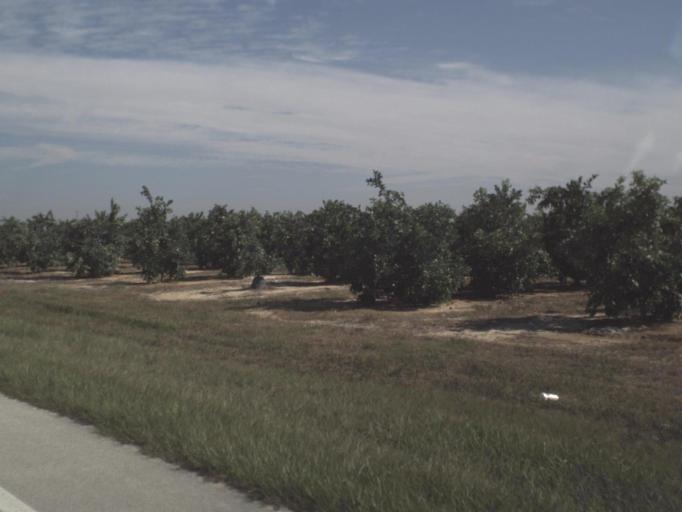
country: US
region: Florida
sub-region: Highlands County
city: Sebring
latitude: 27.5261
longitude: -81.4534
